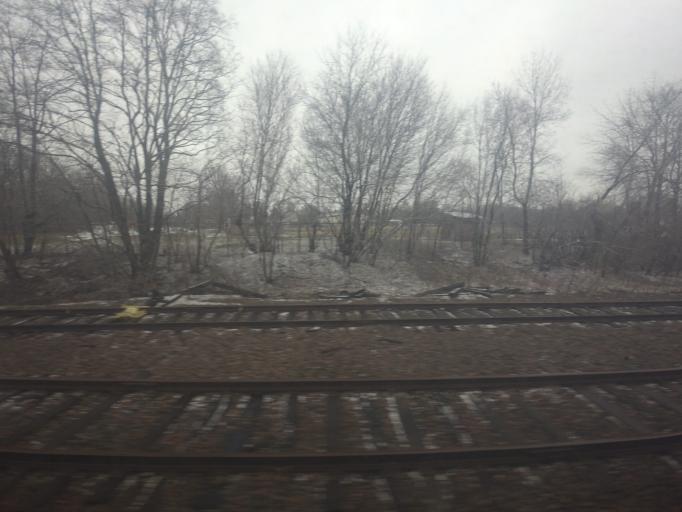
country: CA
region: Ontario
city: Brockville
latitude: 44.5962
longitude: -75.6887
